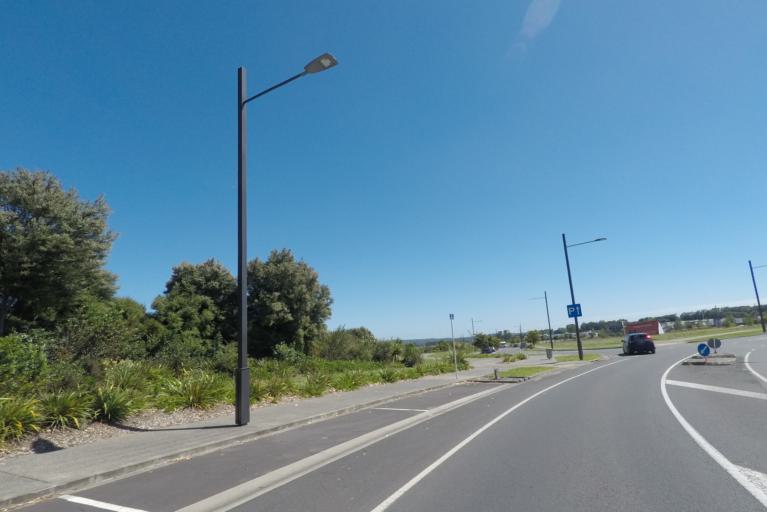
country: NZ
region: Auckland
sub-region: Auckland
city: Rosebank
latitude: -36.8178
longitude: 174.6080
